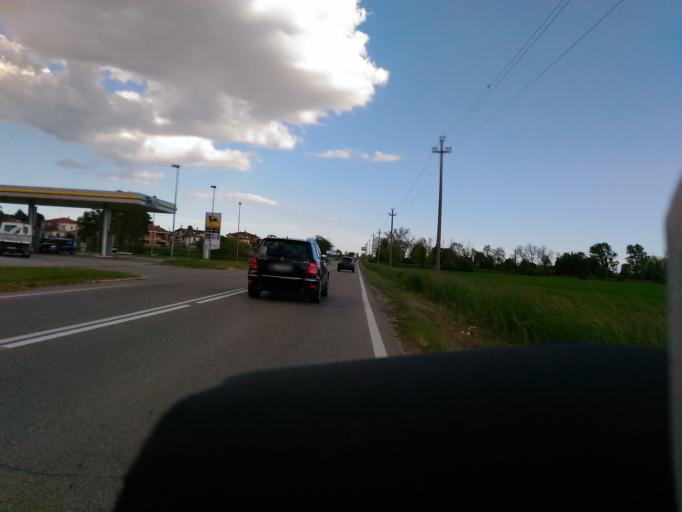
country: IT
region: Lombardy
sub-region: Citta metropolitana di Milano
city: Mediglia
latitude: 45.3939
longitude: 9.3289
